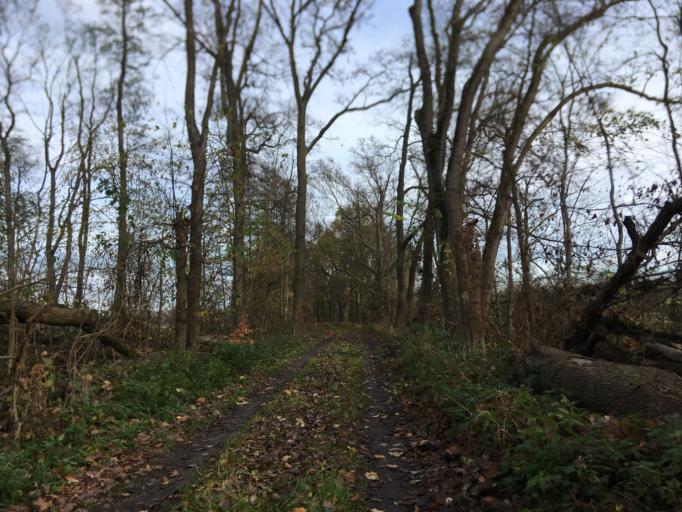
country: DE
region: Brandenburg
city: Schlepzig
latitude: 52.0159
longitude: 13.8578
